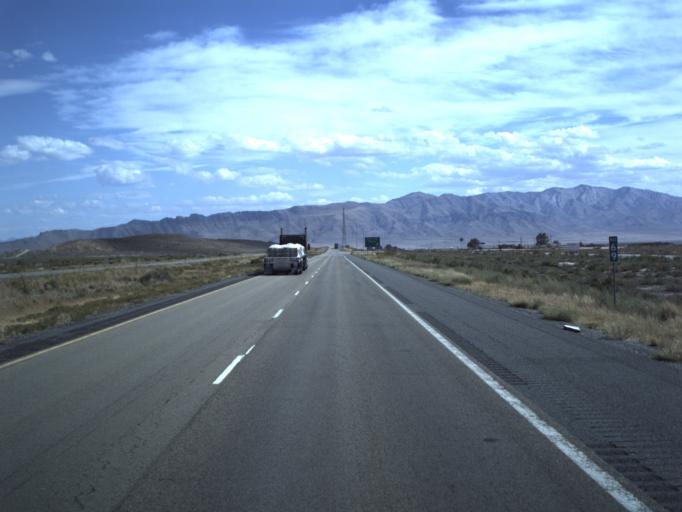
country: US
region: Utah
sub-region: Tooele County
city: Grantsville
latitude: 40.7672
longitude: -112.7897
